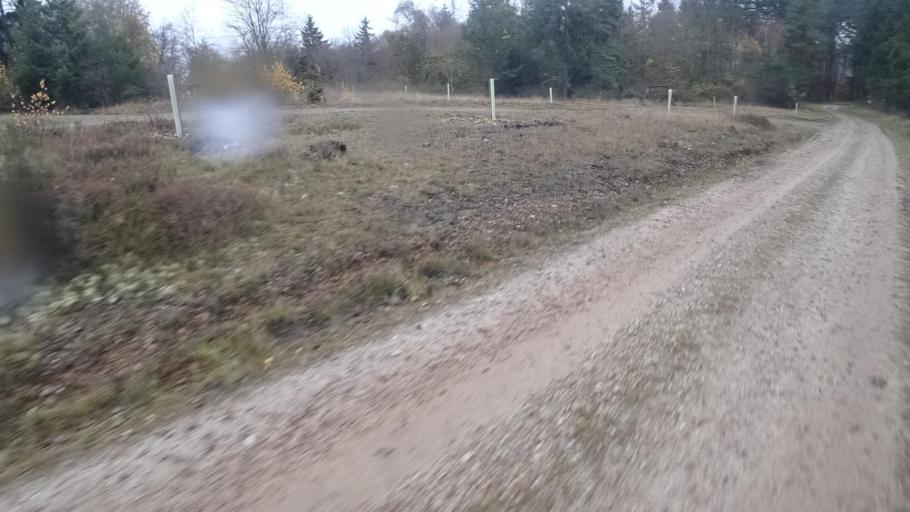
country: DE
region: Rheinland-Pfalz
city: Kestert
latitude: 50.1636
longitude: 7.6608
